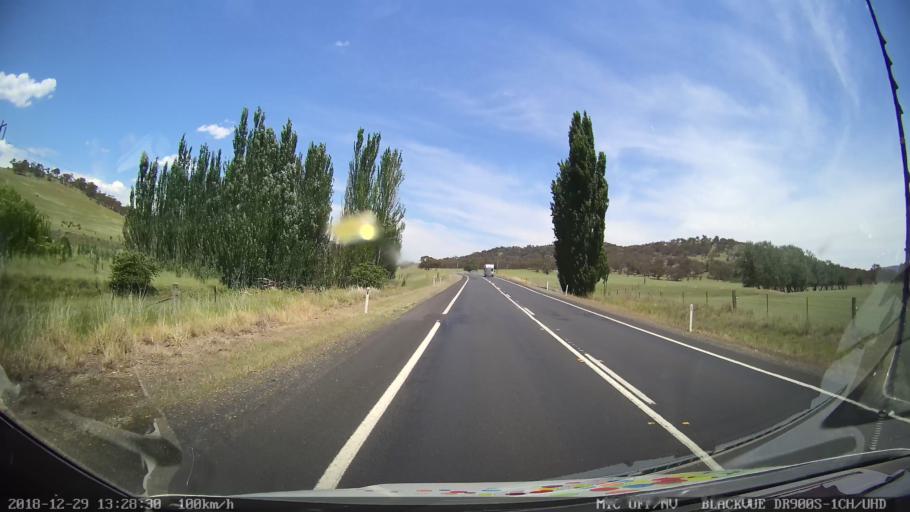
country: AU
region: New South Wales
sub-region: Cooma-Monaro
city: Cooma
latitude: -35.8768
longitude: 149.1609
